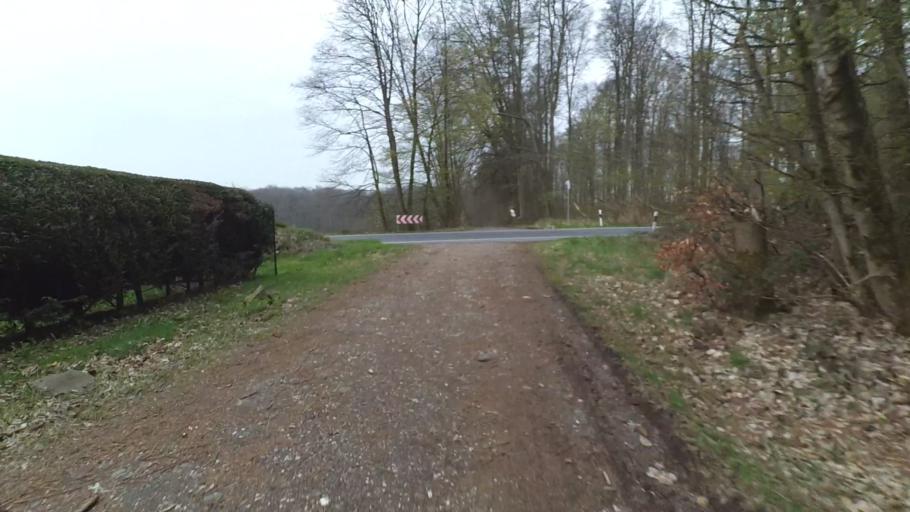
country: DE
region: Rheinland-Pfalz
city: Quirnbach
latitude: 50.5051
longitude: 7.8078
